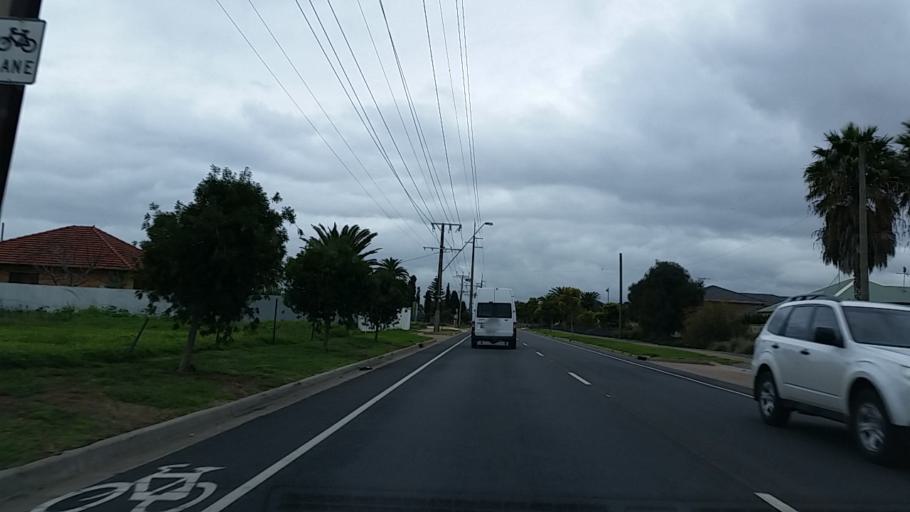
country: AU
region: South Australia
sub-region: Salisbury
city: Salisbury
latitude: -34.7877
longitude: 138.6029
